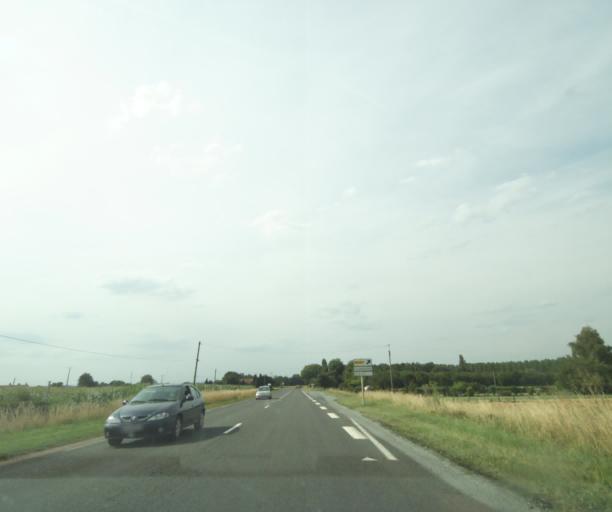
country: FR
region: Pays de la Loire
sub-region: Departement de la Sarthe
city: Ecommoy
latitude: 47.8511
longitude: 0.2545
